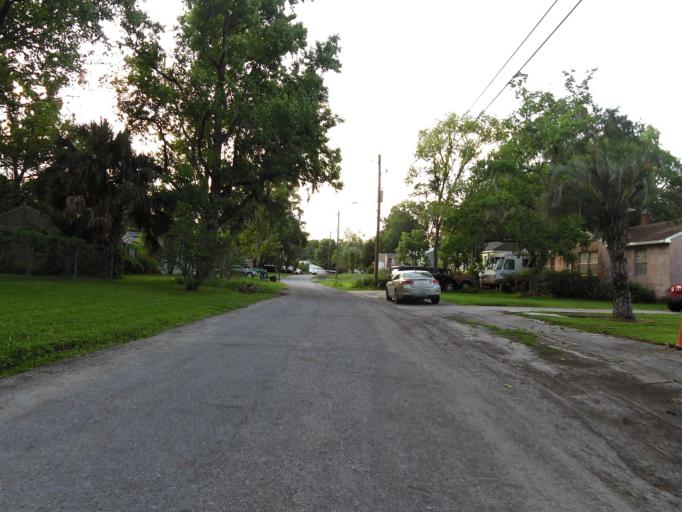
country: US
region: Florida
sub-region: Duval County
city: Jacksonville
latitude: 30.3021
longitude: -81.6235
